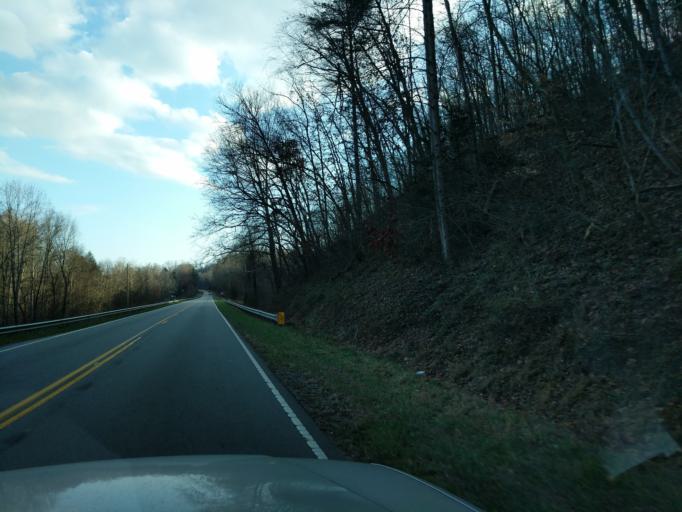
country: US
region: North Carolina
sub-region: McDowell County
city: West Marion
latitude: 35.5715
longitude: -81.9737
